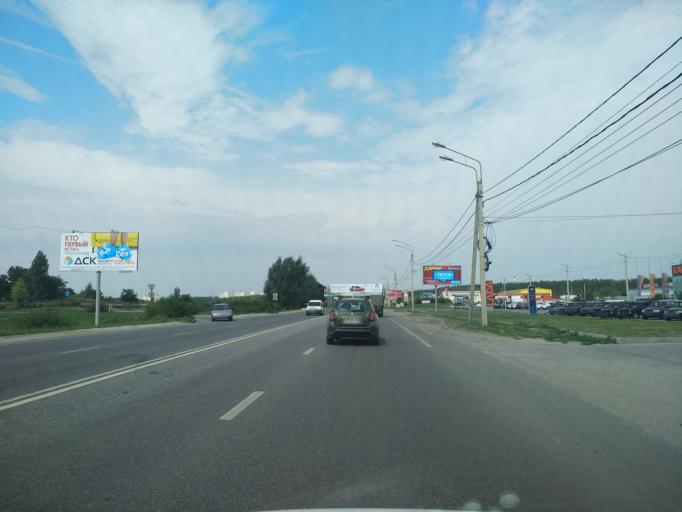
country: RU
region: Voronezj
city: Somovo
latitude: 51.6793
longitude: 39.2900
